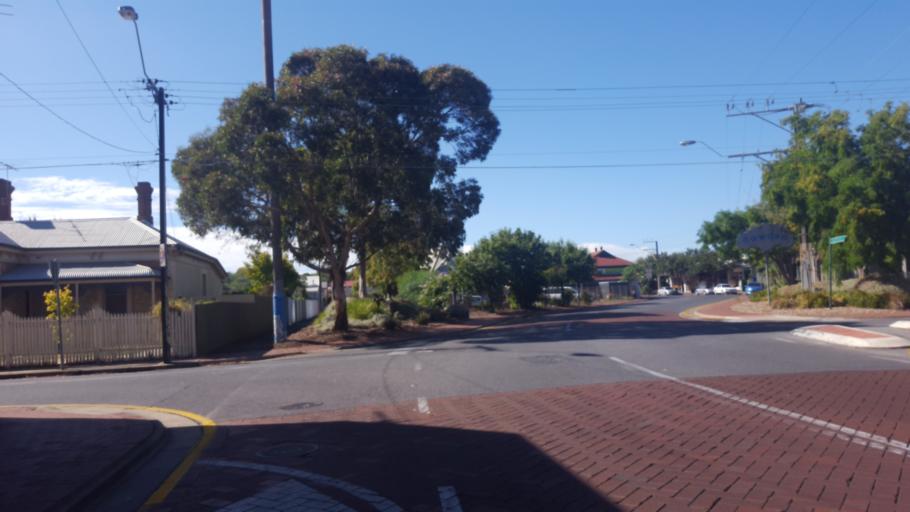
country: AU
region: South Australia
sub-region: Adelaide
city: North Adelaide
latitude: -34.8994
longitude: 138.5799
